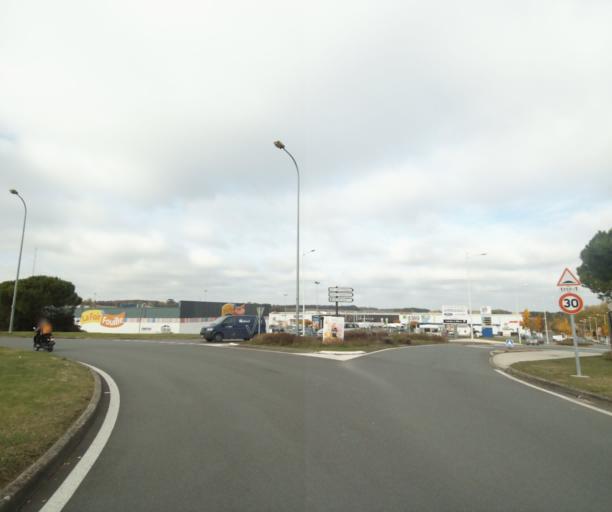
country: FR
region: Poitou-Charentes
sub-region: Departement de la Charente-Maritime
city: Saintes
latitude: 45.7459
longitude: -0.6744
